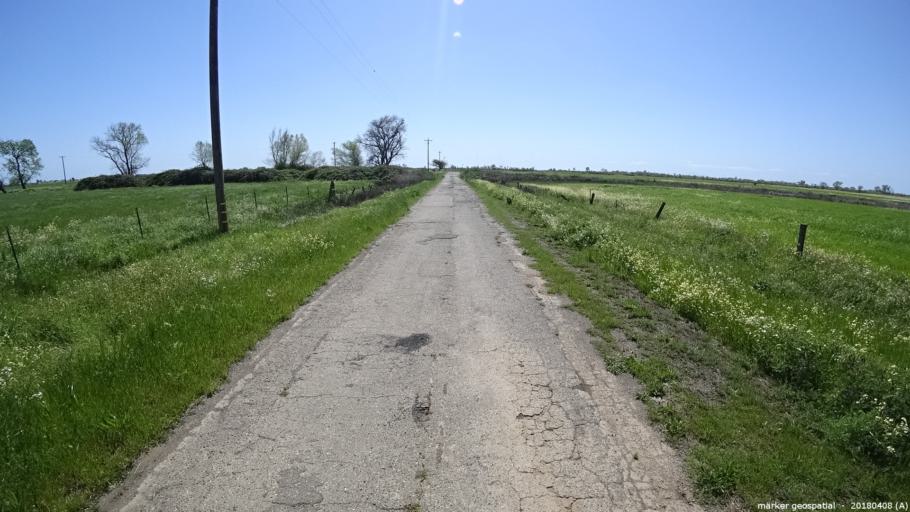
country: US
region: California
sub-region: Sacramento County
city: Laguna
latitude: 38.3591
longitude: -121.4822
